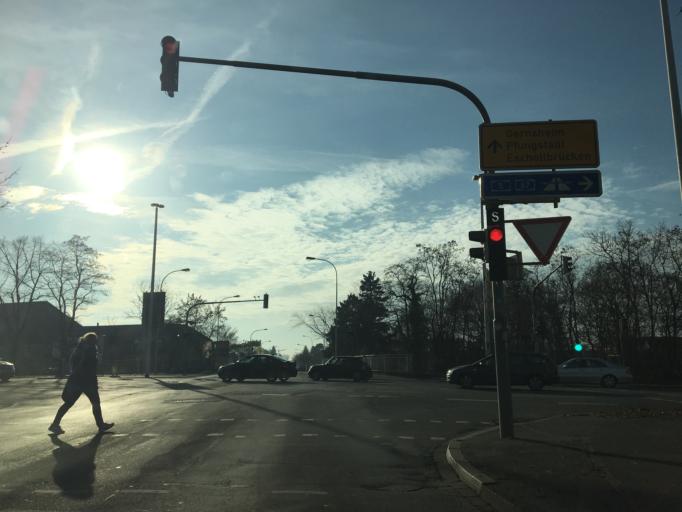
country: DE
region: Hesse
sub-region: Regierungsbezirk Darmstadt
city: Darmstadt
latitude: 49.8592
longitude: 8.6353
